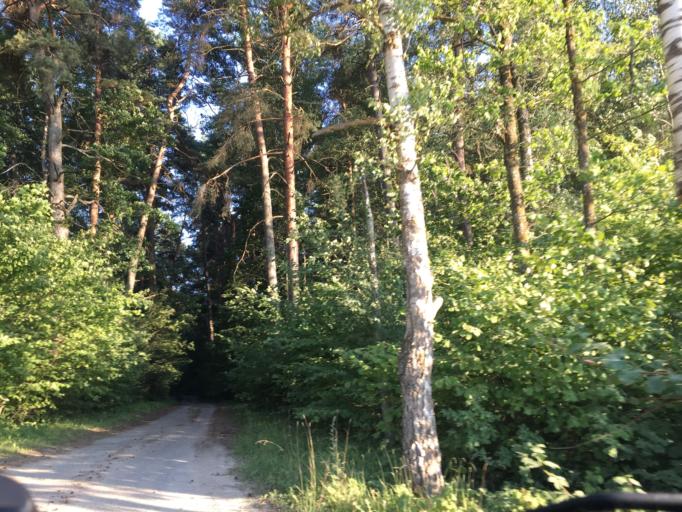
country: LV
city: Tervete
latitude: 56.4732
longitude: 23.3702
